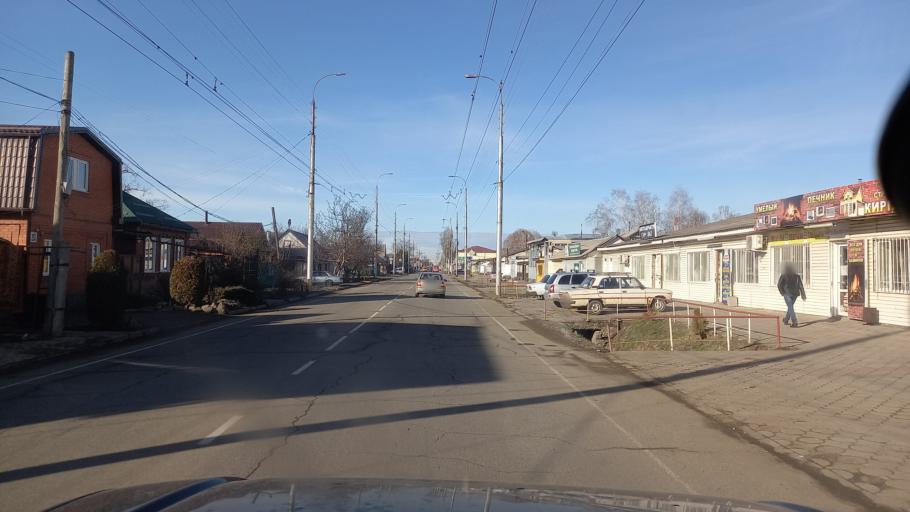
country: RU
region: Adygeya
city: Maykop
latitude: 44.6213
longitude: 40.1019
